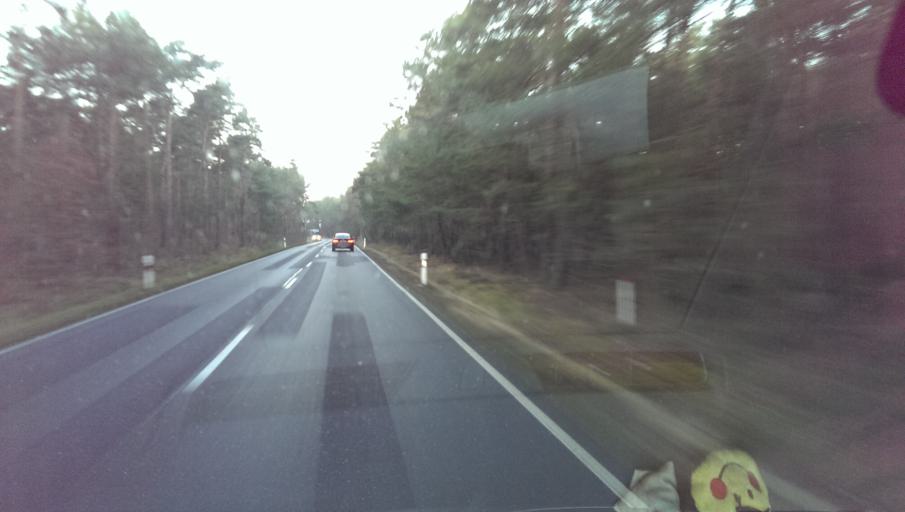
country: DE
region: Saxony-Anhalt
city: Holzdorf
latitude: 51.7815
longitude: 13.1944
